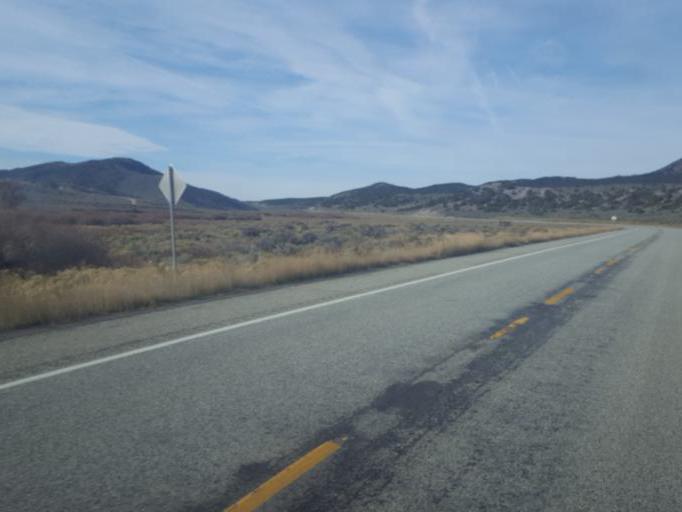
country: US
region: Colorado
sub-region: Costilla County
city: San Luis
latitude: 37.5153
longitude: -105.3067
